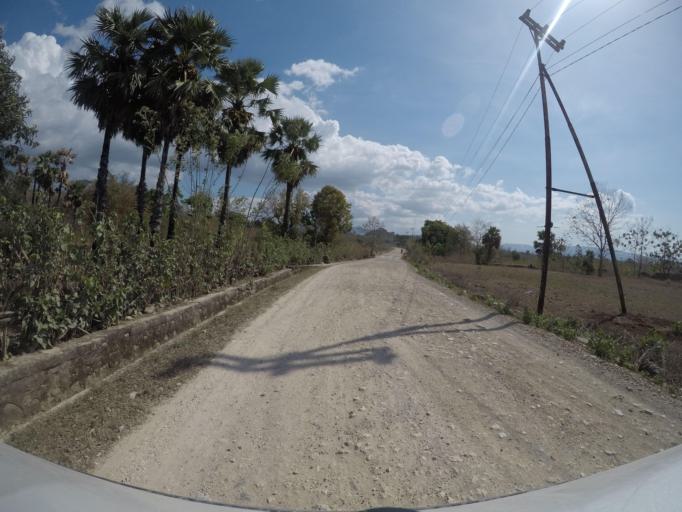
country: TL
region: Bobonaro
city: Maliana
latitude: -8.9951
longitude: 125.2013
